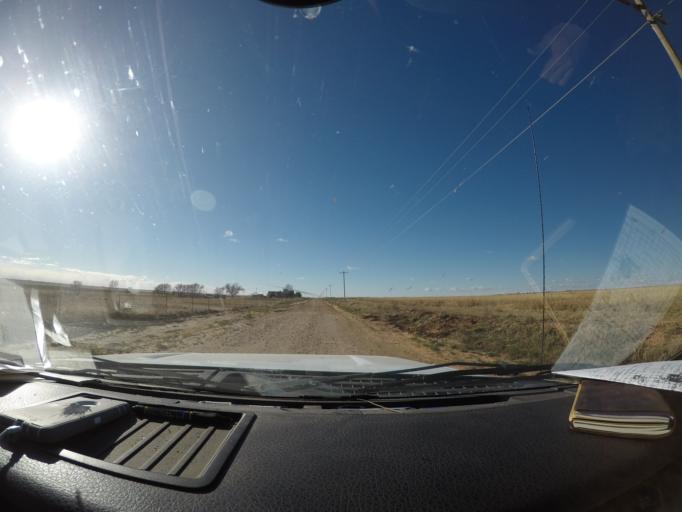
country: US
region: New Mexico
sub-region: Curry County
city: Clovis
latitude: 34.5648
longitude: -103.2553
